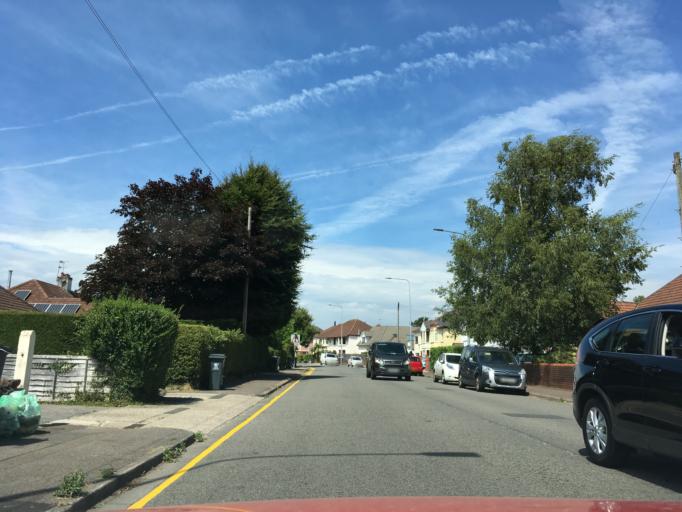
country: GB
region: Wales
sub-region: Cardiff
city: Cardiff
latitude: 51.5157
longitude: -3.1831
